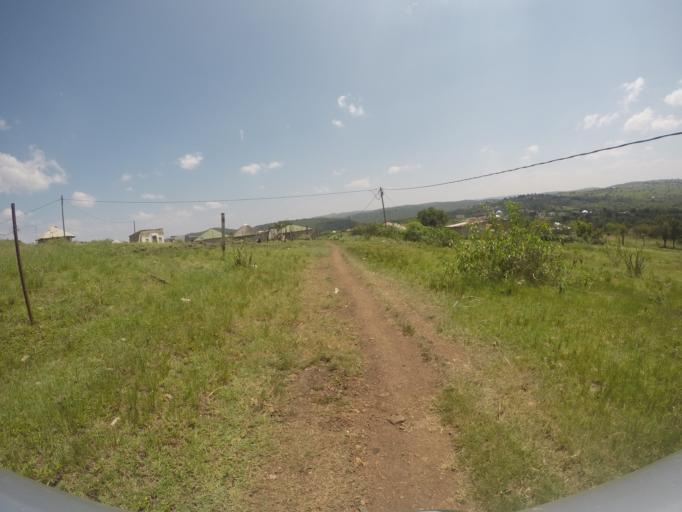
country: ZA
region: KwaZulu-Natal
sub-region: uThungulu District Municipality
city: Empangeni
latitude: -28.5957
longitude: 31.7373
